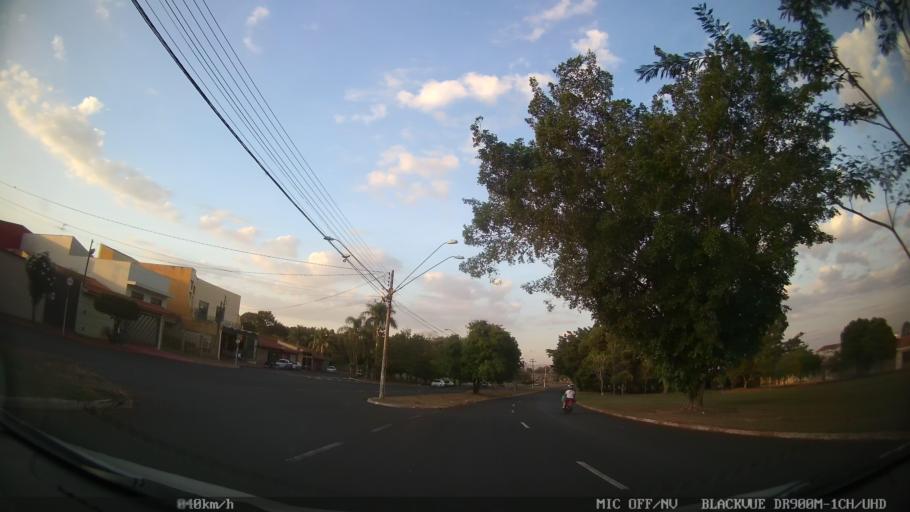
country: BR
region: Sao Paulo
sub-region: Ribeirao Preto
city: Ribeirao Preto
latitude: -21.1311
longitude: -47.8393
